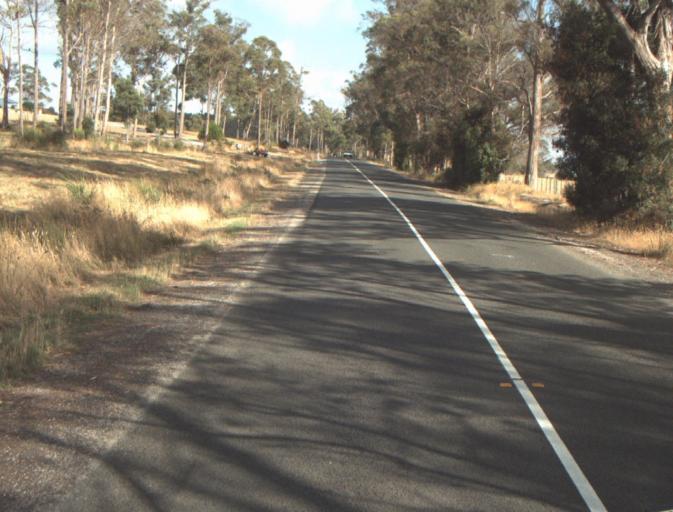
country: AU
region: Tasmania
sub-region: Dorset
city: Bridport
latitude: -41.1159
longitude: 147.2037
